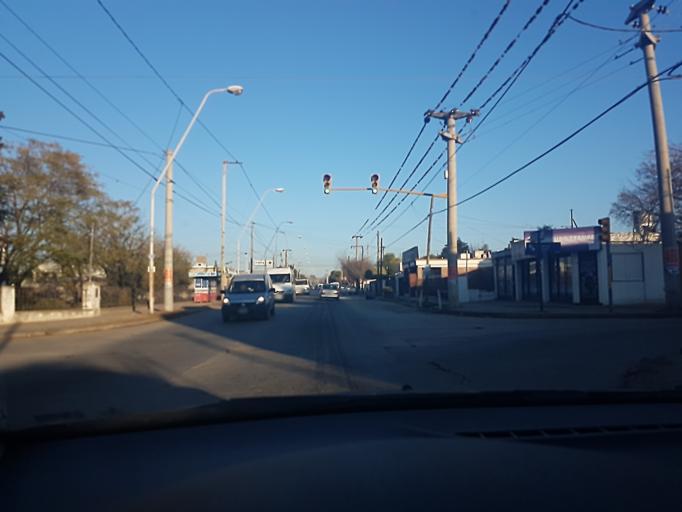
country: AR
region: Cordoba
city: Villa Allende
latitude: -31.3433
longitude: -64.2384
